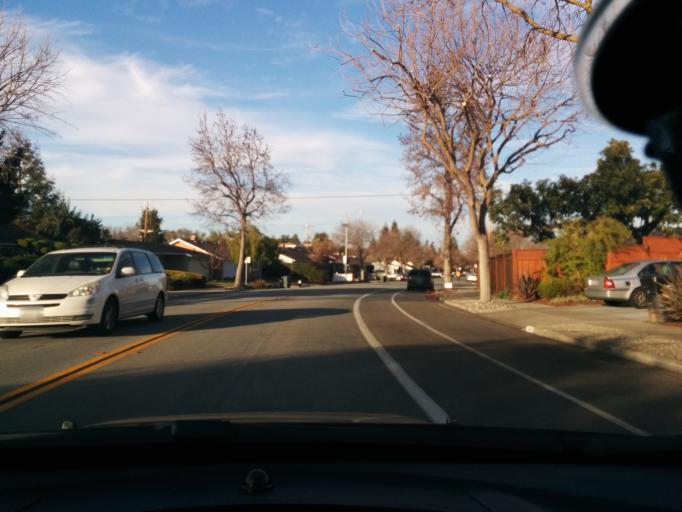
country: US
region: California
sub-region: Santa Clara County
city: Sunnyvale
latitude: 37.3671
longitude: -122.0623
